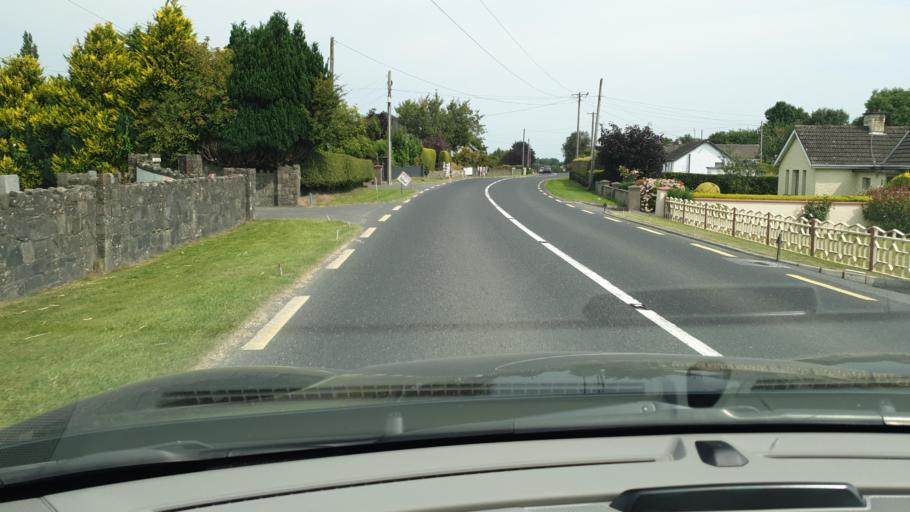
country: IE
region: Leinster
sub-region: An Mhi
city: Kells
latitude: 53.7110
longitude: -6.9074
